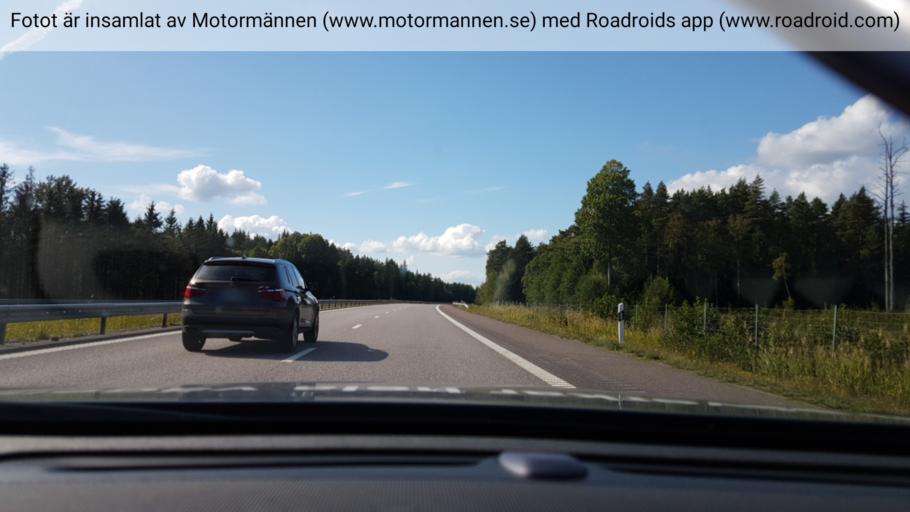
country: SE
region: Soedermanland
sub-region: Nykopings Kommun
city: Svalsta
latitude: 58.7574
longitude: 16.8321
